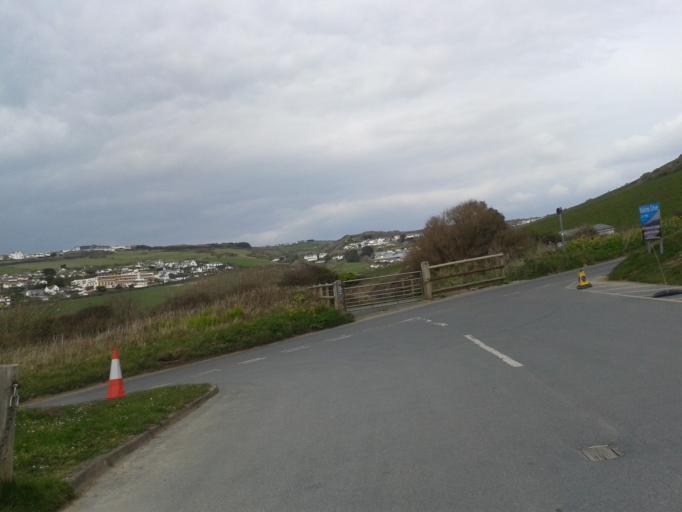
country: GB
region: England
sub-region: Devon
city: Braunton
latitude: 51.1675
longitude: -4.2057
